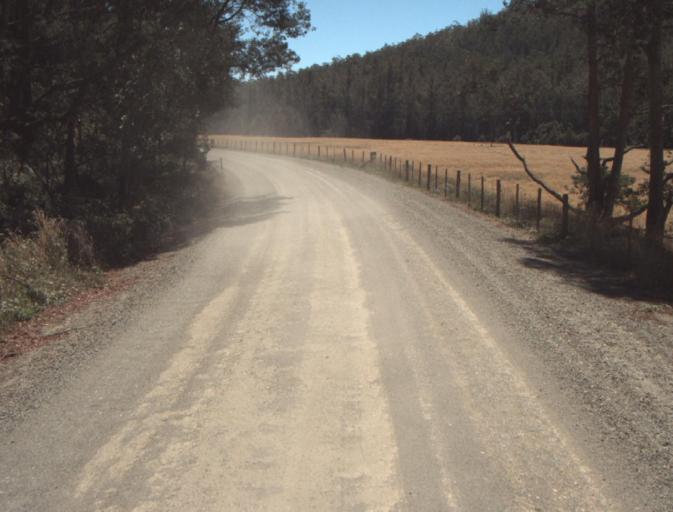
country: AU
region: Tasmania
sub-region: Dorset
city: Scottsdale
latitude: -41.2904
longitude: 147.3925
